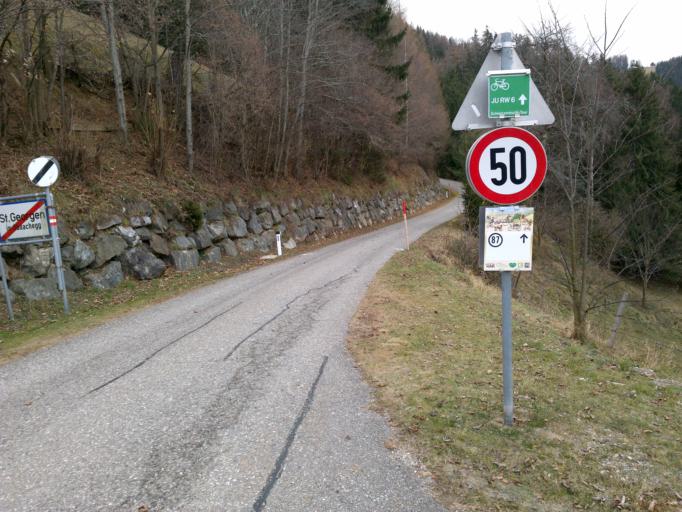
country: AT
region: Styria
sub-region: Politischer Bezirk Murtal
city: Eppenstein
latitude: 47.0791
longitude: 14.7399
